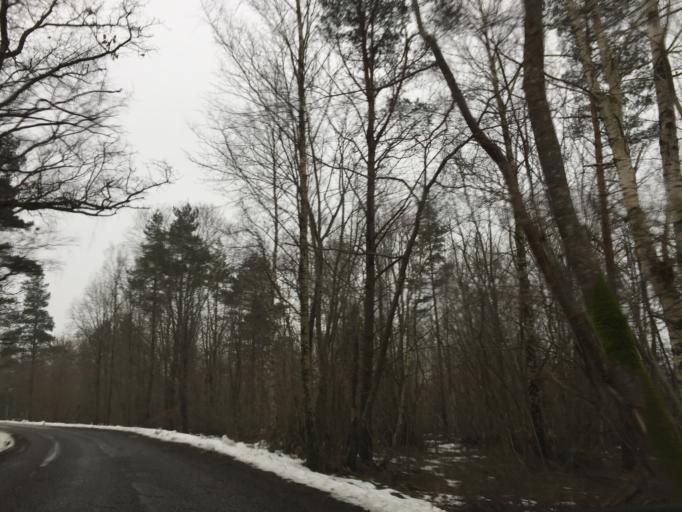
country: EE
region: Saare
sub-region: Kuressaare linn
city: Kuressaare
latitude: 58.2760
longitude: 22.5702
